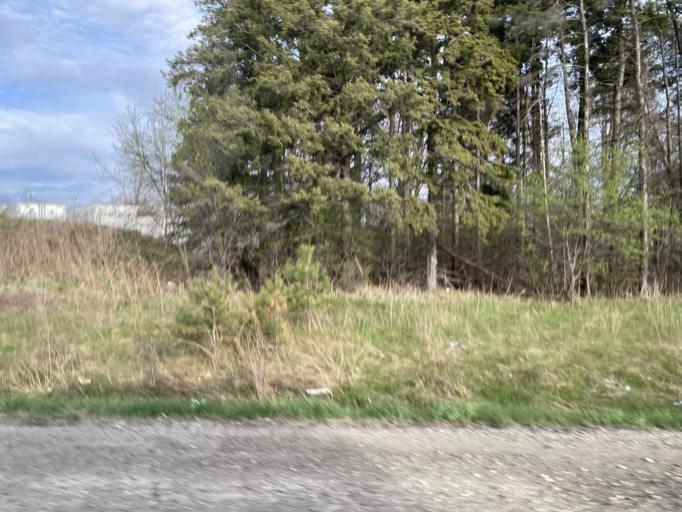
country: CA
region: Ontario
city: Waterloo
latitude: 43.4669
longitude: -80.4036
